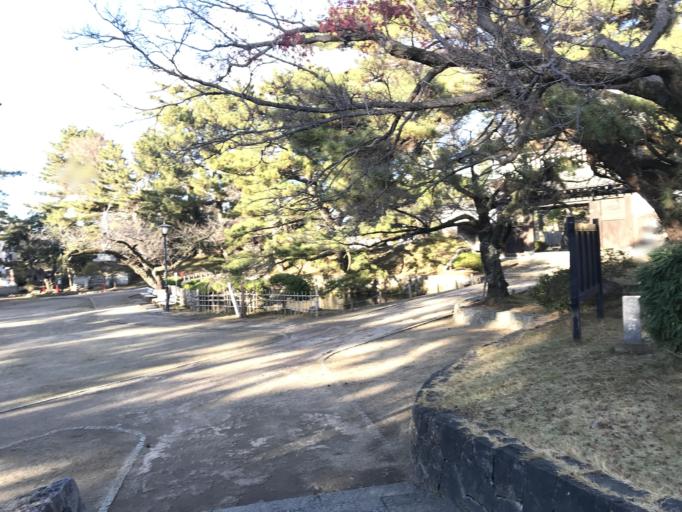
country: JP
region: Ibaraki
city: Naka
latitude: 36.0843
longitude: 140.1982
